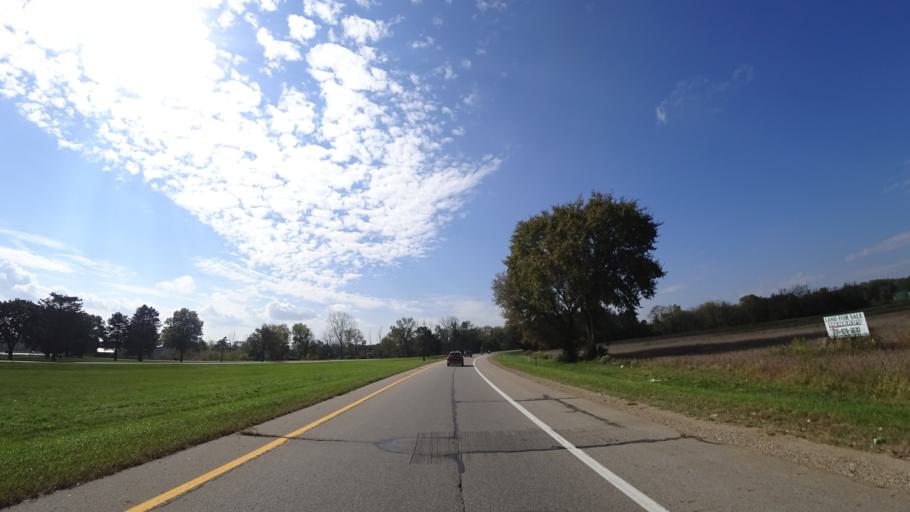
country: US
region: Michigan
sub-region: Saint Joseph County
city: Three Rivers
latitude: 41.9287
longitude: -85.6531
